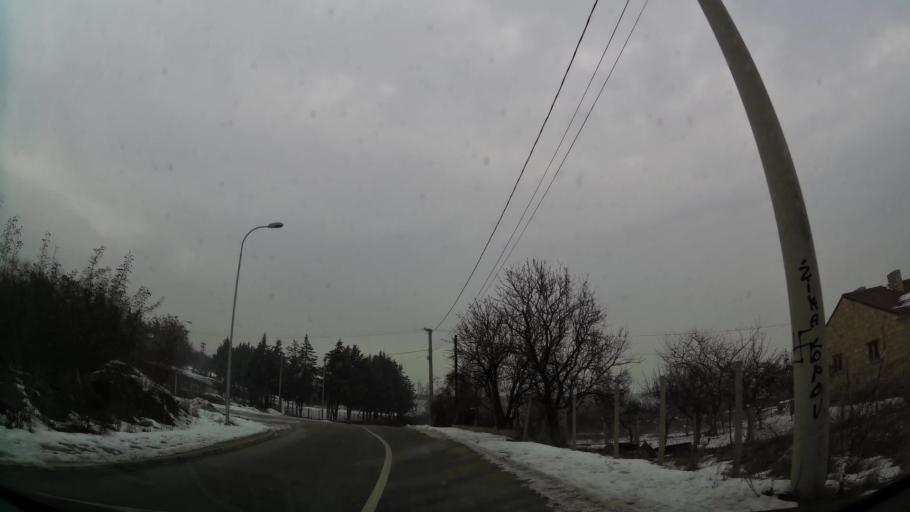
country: MK
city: Kondovo
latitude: 42.0535
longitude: 21.3488
